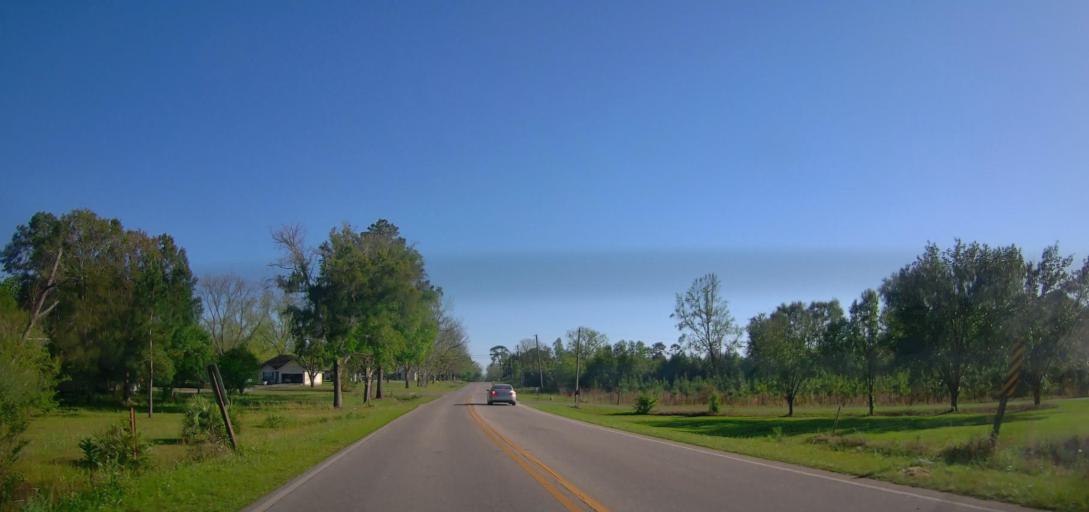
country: US
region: Georgia
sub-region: Ben Hill County
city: Fitzgerald
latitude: 31.7276
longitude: -83.2353
